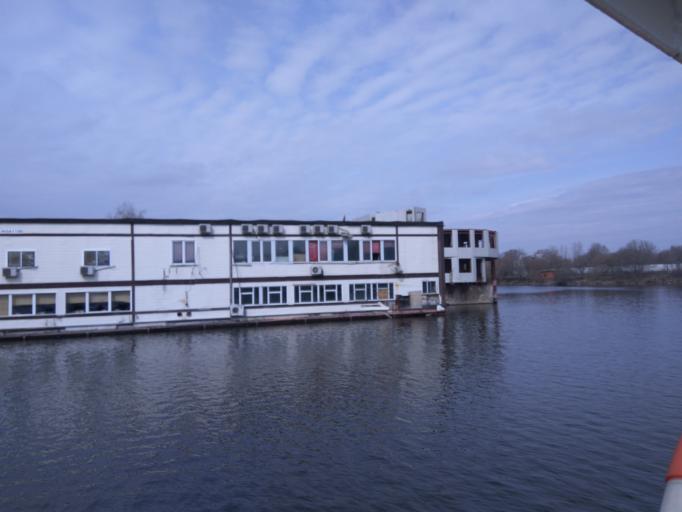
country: RU
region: Moscow
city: Kolomenskoye
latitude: 55.6874
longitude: 37.7030
